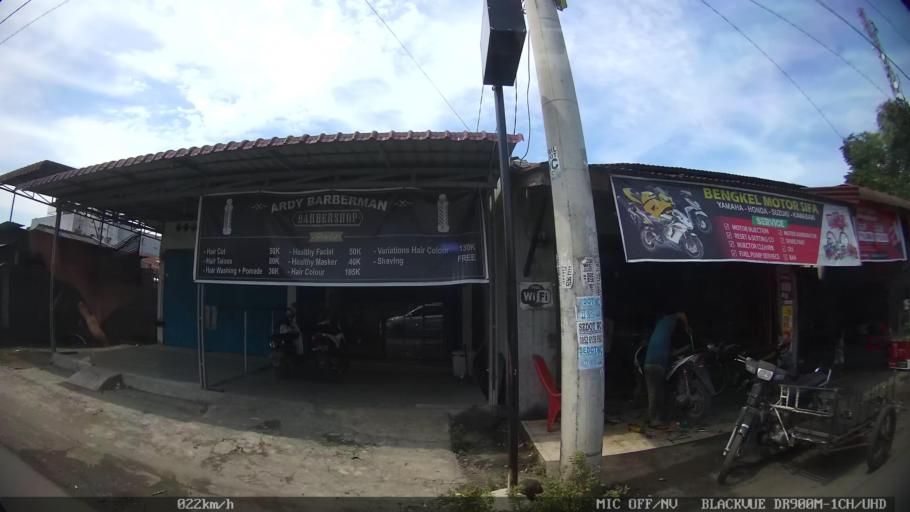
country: ID
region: North Sumatra
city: Labuhan Deli
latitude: 3.6887
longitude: 98.6575
